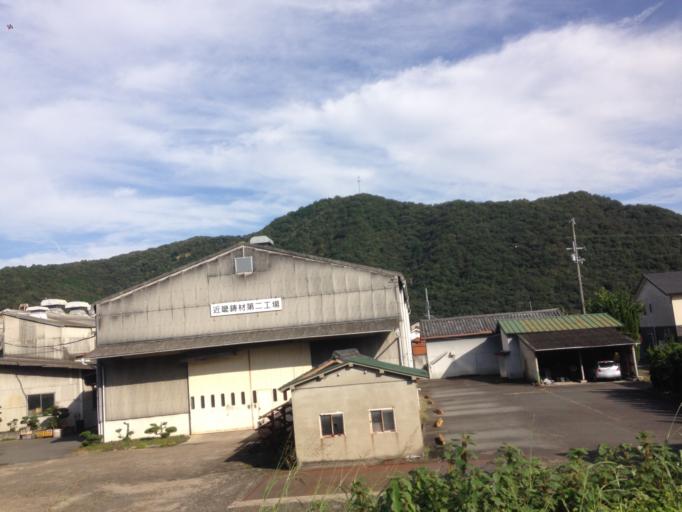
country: JP
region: Hyogo
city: Tatsunocho-tominaga
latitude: 34.8728
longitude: 134.5518
